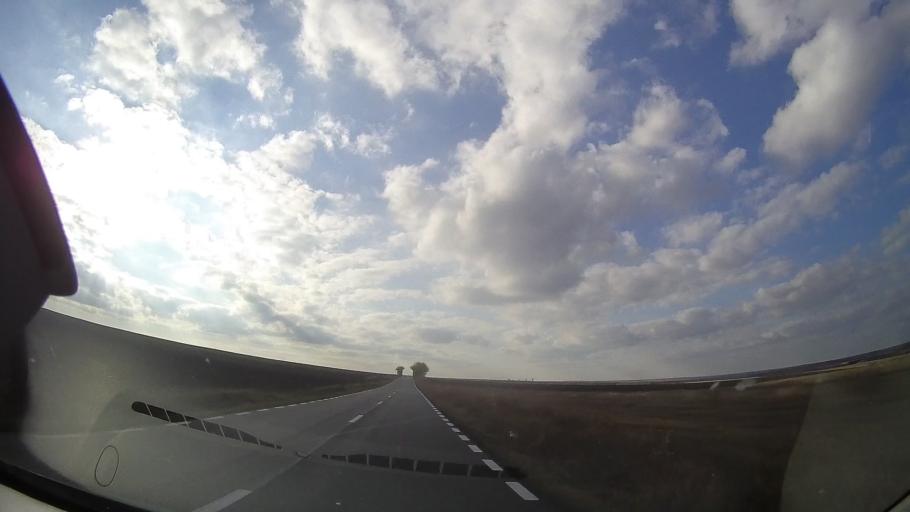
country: RO
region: Constanta
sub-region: Comuna Albesti
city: Albesti
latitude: 43.8079
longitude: 28.3966
